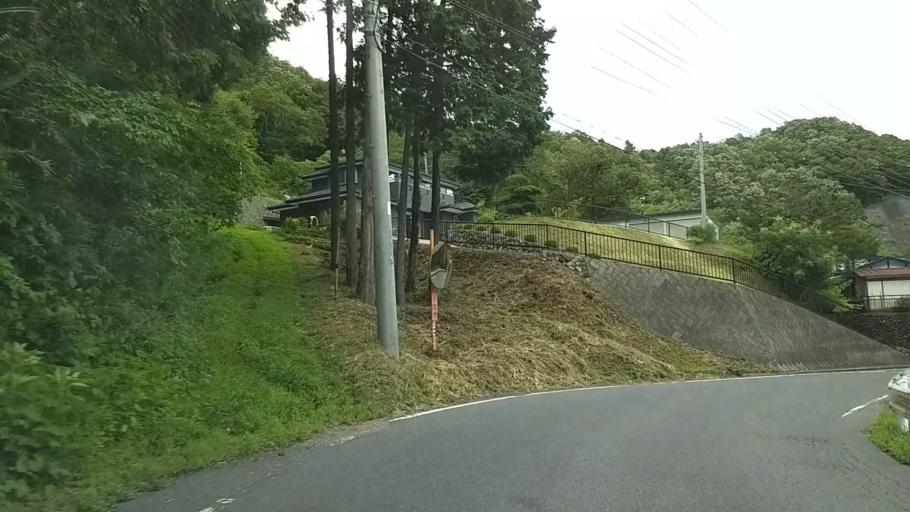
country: JP
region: Yamanashi
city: Uenohara
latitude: 35.5691
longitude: 139.0828
